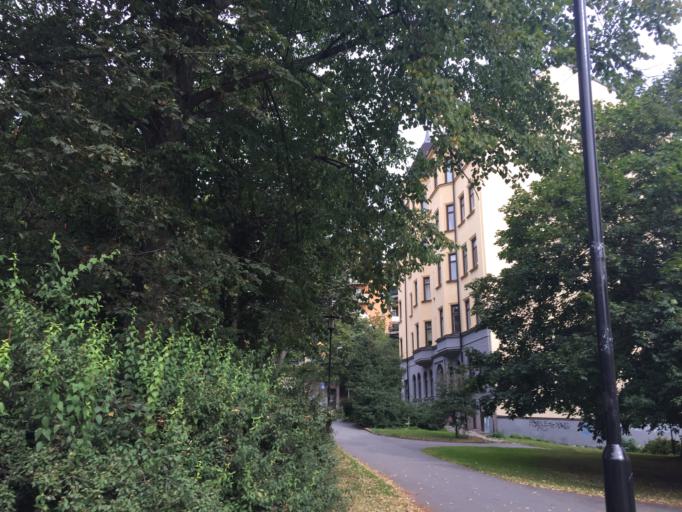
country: SE
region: Stockholm
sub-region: Stockholms Kommun
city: Arsta
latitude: 59.3177
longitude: 18.0460
